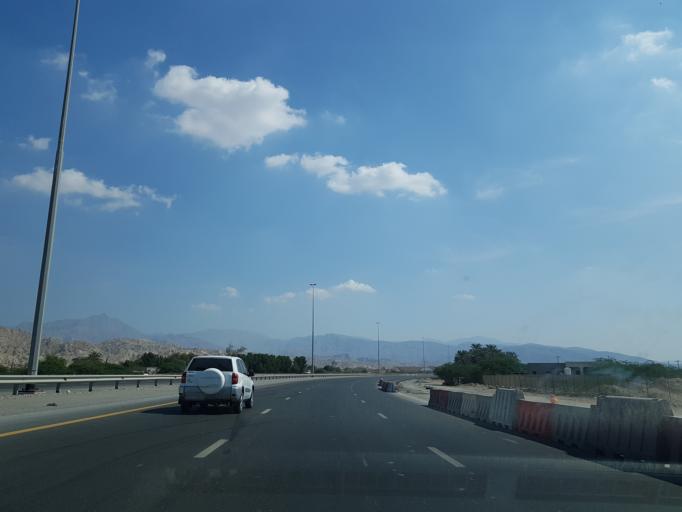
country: AE
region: Ra's al Khaymah
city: Ras al-Khaimah
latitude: 25.8264
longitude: 56.0208
